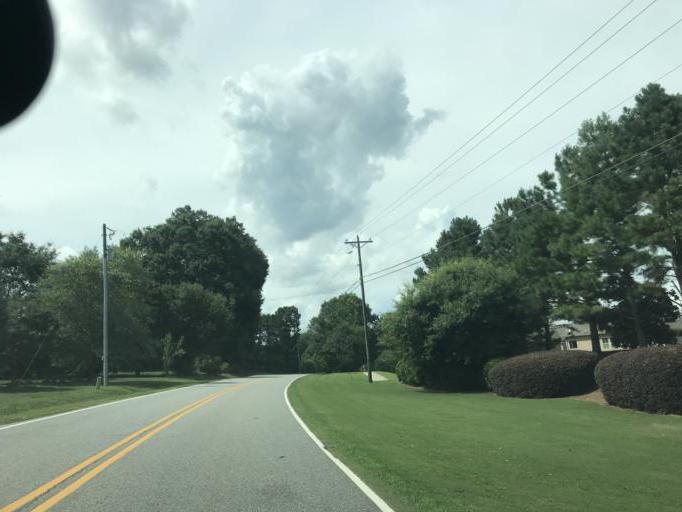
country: US
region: Georgia
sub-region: Forsyth County
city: Cumming
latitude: 34.2342
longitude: -84.2448
